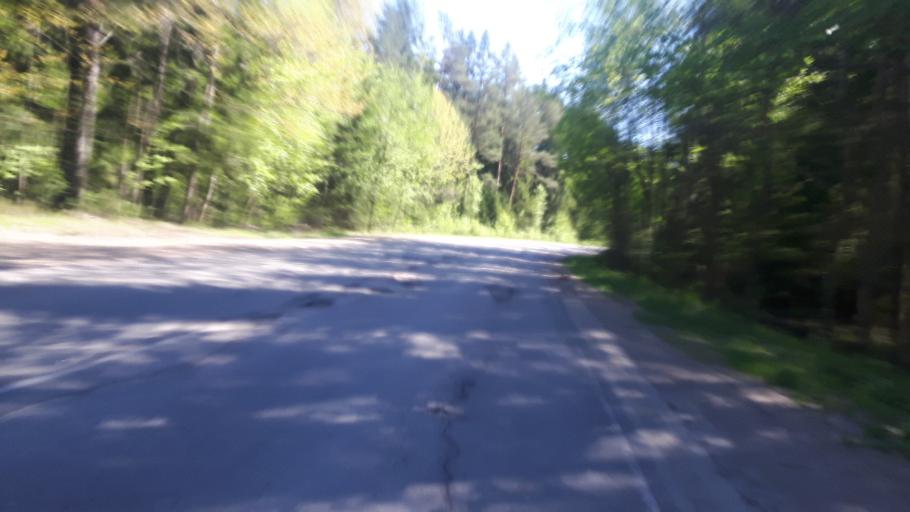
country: RU
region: Leningrad
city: Glebychevo
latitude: 60.2383
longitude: 29.0032
